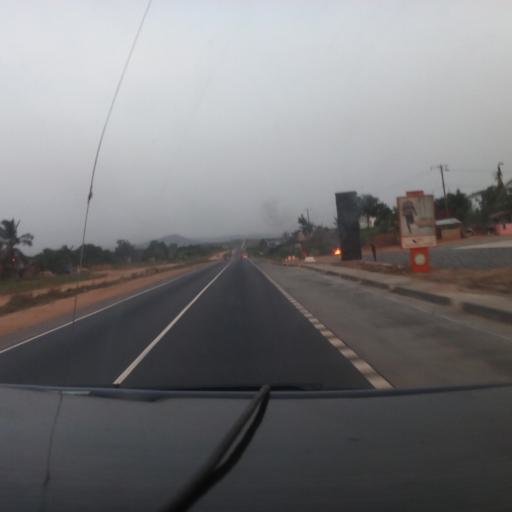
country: GH
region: Eastern
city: Nsawam
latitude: 5.8752
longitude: -0.3708
